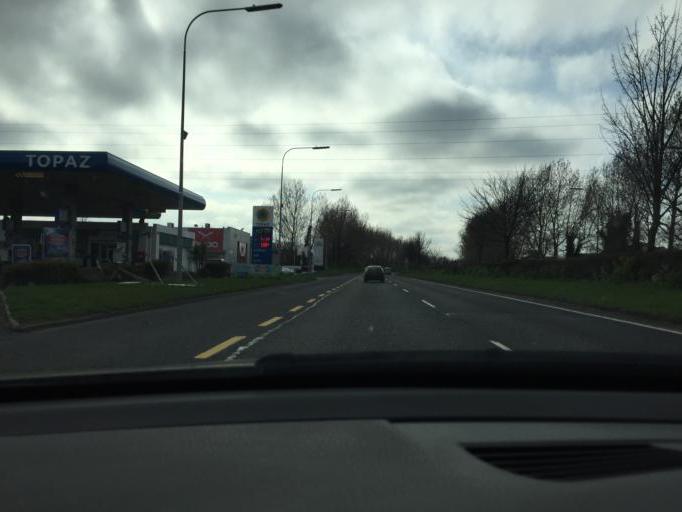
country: IE
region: Leinster
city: Firhouse
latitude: 53.2872
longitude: -6.3452
